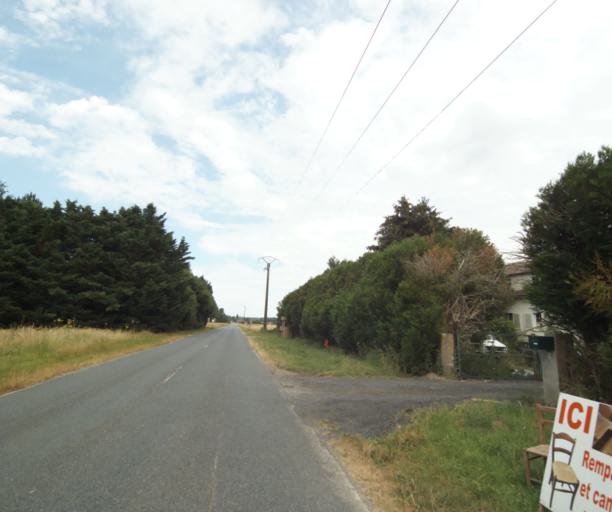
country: FR
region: Ile-de-France
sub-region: Departement de Seine-et-Marne
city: Arbonne-la-Foret
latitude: 48.4247
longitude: 2.5764
